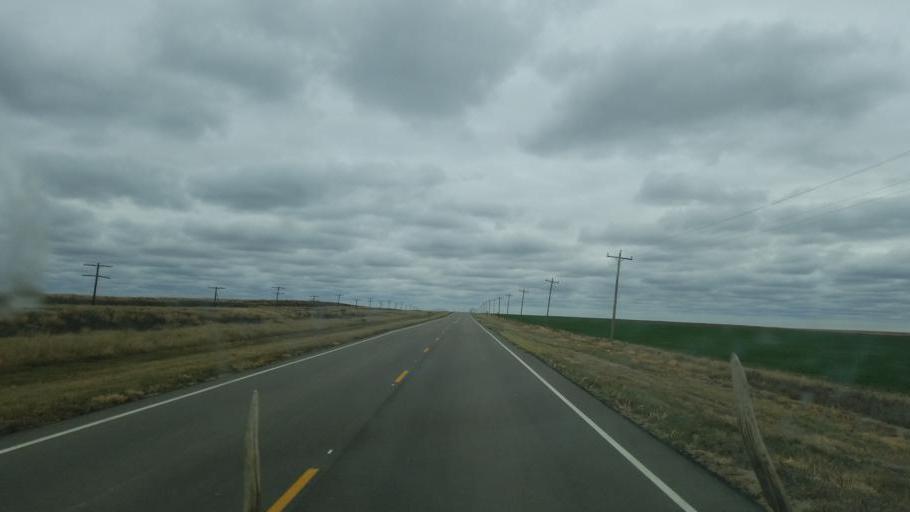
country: US
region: Colorado
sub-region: Kiowa County
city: Eads
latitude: 38.5012
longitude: -103.0076
